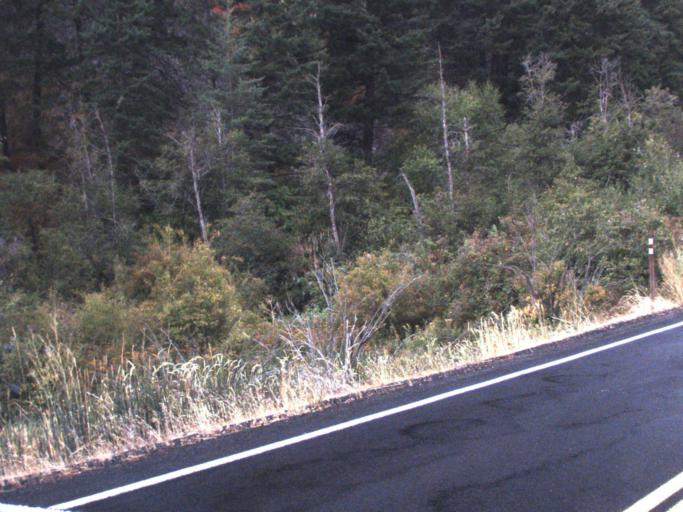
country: US
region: Washington
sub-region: Spokane County
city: Medical Lake
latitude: 47.7532
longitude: -117.8892
